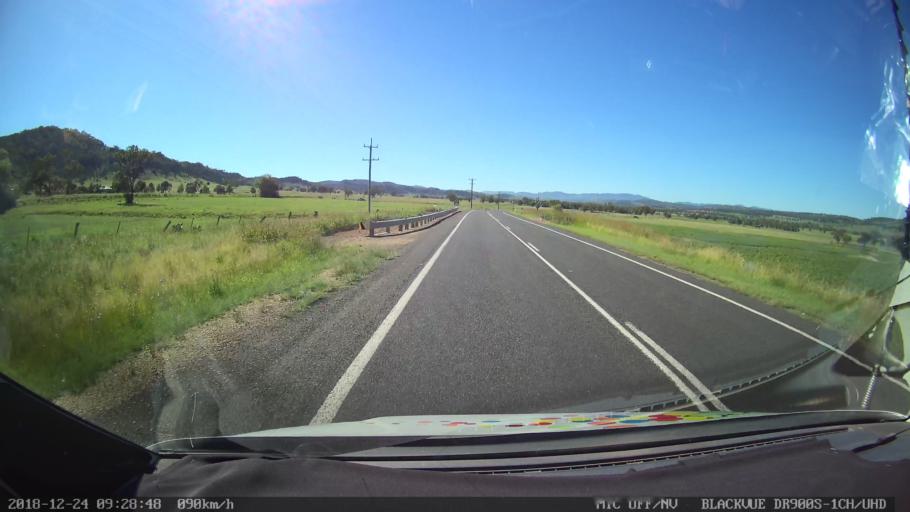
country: AU
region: New South Wales
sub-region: Liverpool Plains
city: Quirindi
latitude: -31.5420
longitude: 150.6916
